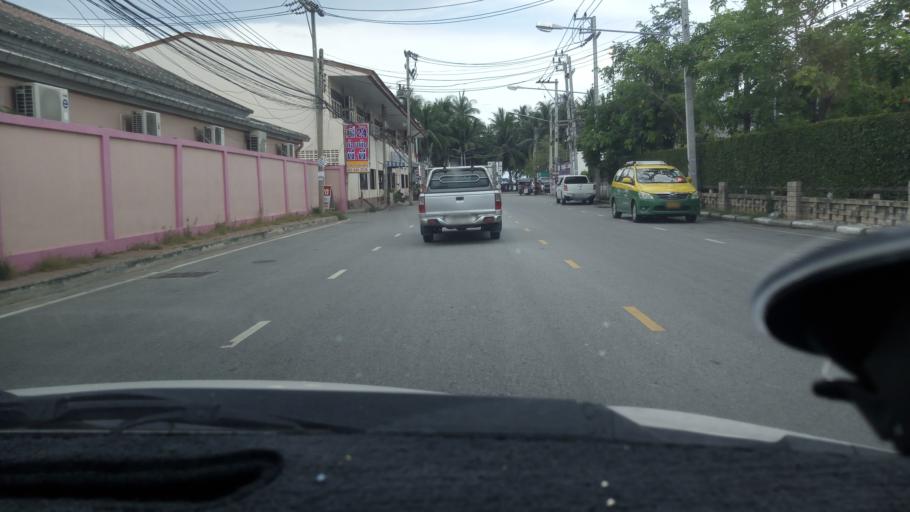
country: TH
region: Chon Buri
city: Chon Buri
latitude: 13.2906
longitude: 100.9112
